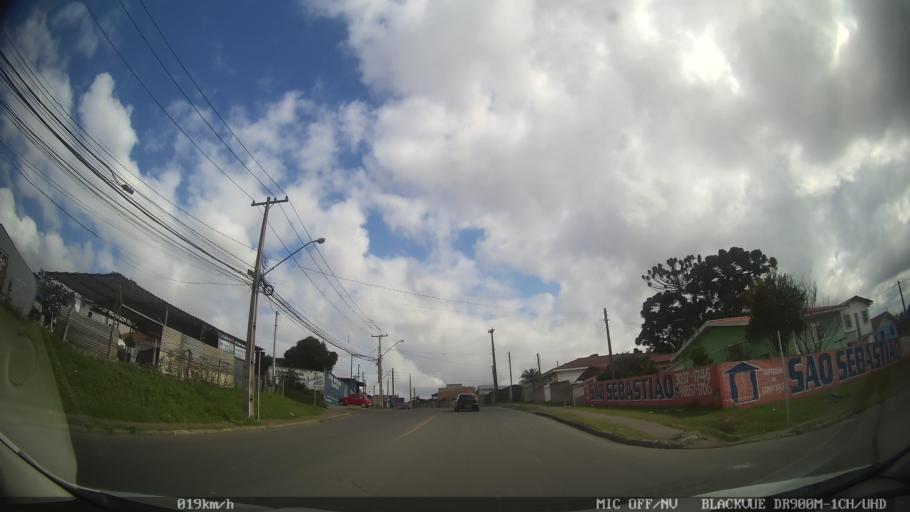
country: BR
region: Parana
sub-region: Colombo
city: Colombo
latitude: -25.3450
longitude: -49.1899
